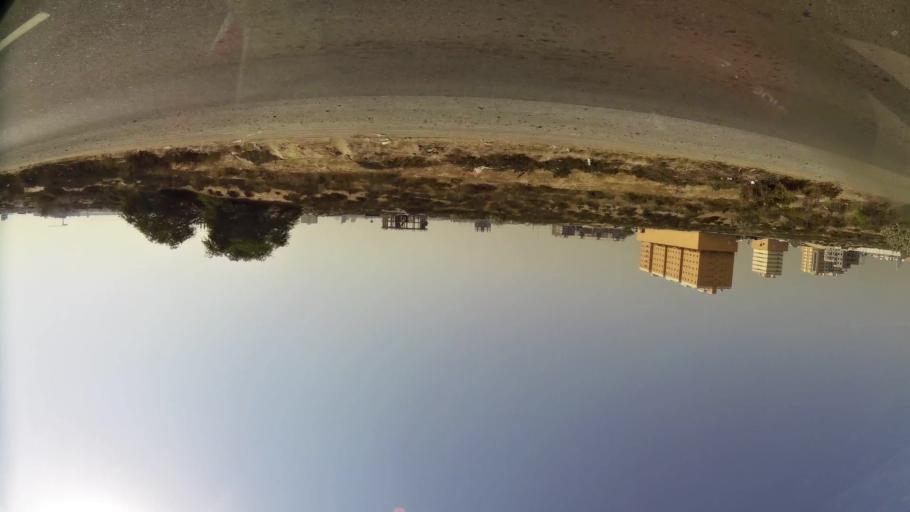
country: AE
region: Ajman
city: Ajman
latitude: 25.4208
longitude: 55.5370
